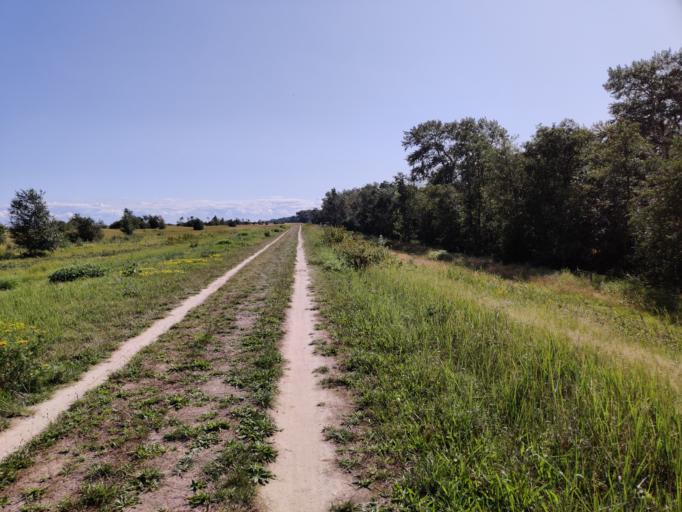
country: DK
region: Zealand
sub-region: Guldborgsund Kommune
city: Nykobing Falster
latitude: 54.6297
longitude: 11.9618
